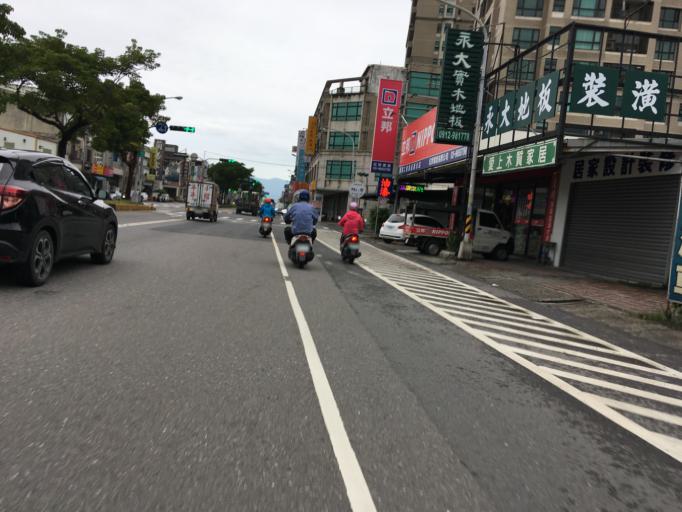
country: TW
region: Taiwan
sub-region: Yilan
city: Yilan
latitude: 24.6897
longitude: 121.7704
